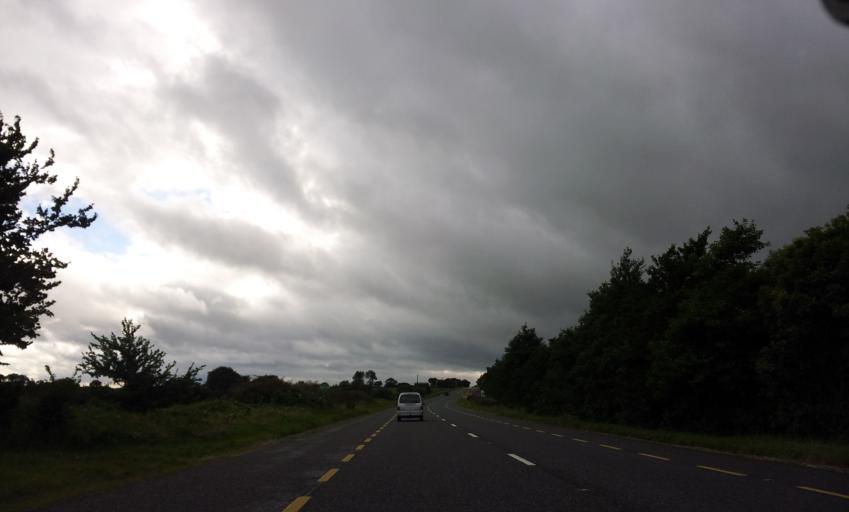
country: IE
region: Munster
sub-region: County Cork
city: Youghal
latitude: 51.9383
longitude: -7.9388
